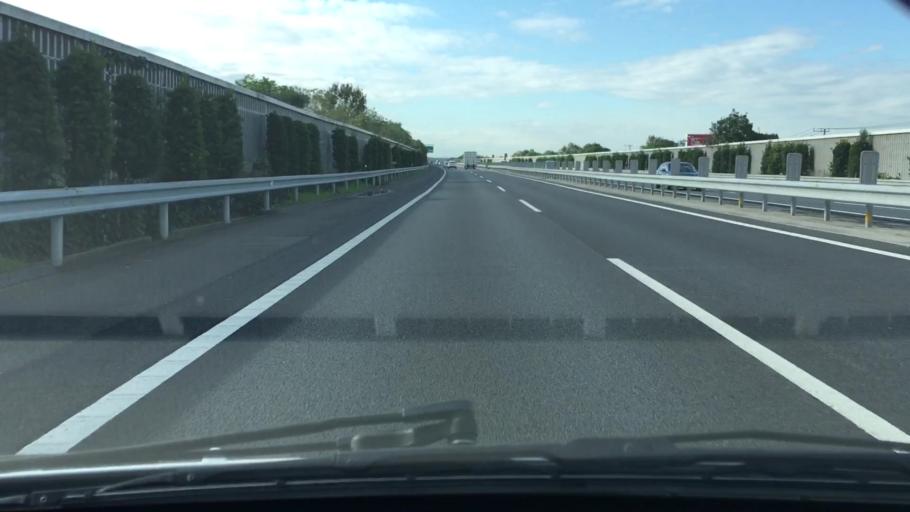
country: JP
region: Chiba
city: Ichihara
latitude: 35.5051
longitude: 140.1039
